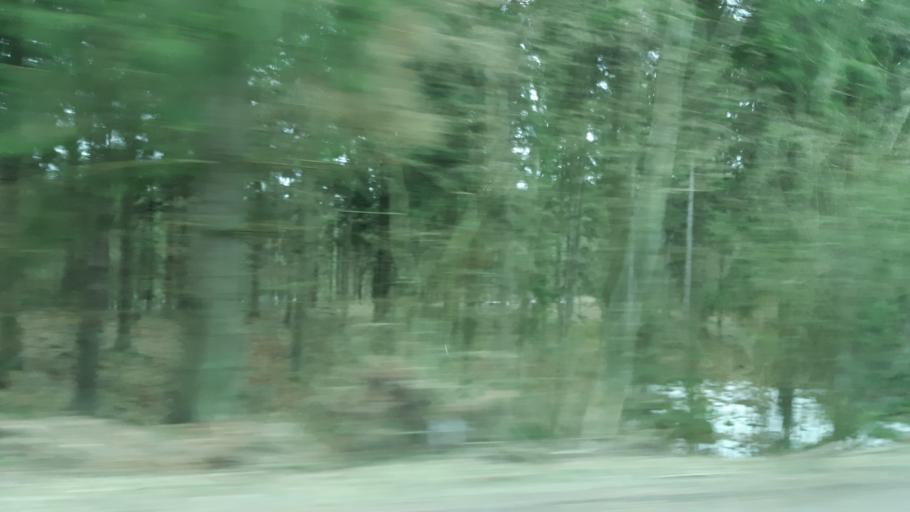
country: PL
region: Podlasie
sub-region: Suwalki
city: Suwalki
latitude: 54.3016
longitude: 22.9573
